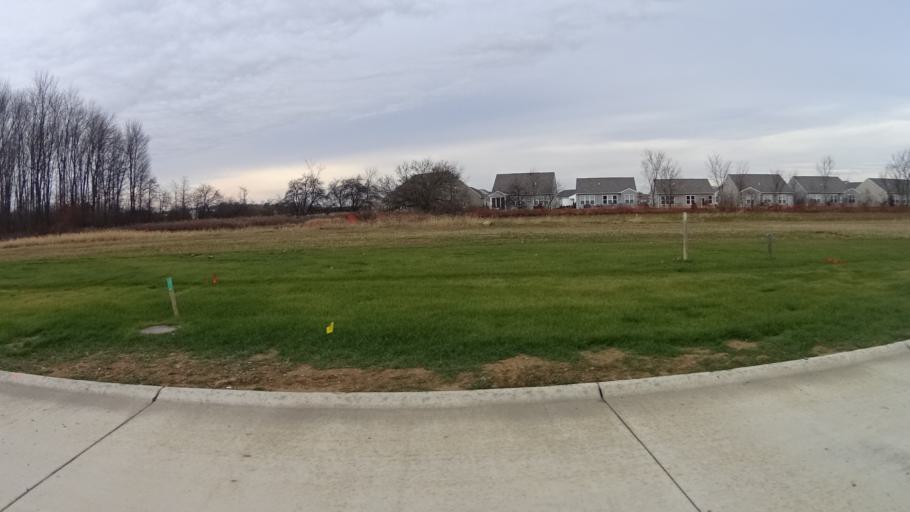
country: US
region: Ohio
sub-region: Lorain County
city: North Ridgeville
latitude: 41.3523
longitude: -82.0420
